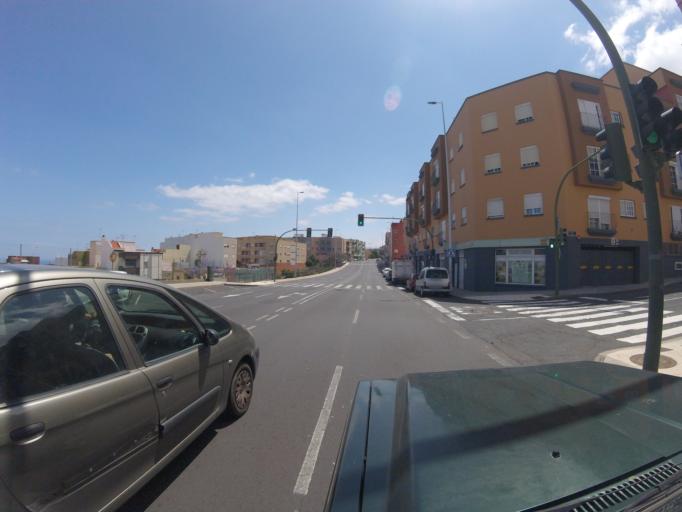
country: ES
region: Canary Islands
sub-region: Provincia de Santa Cruz de Tenerife
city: La Laguna
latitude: 28.4365
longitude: -16.3071
